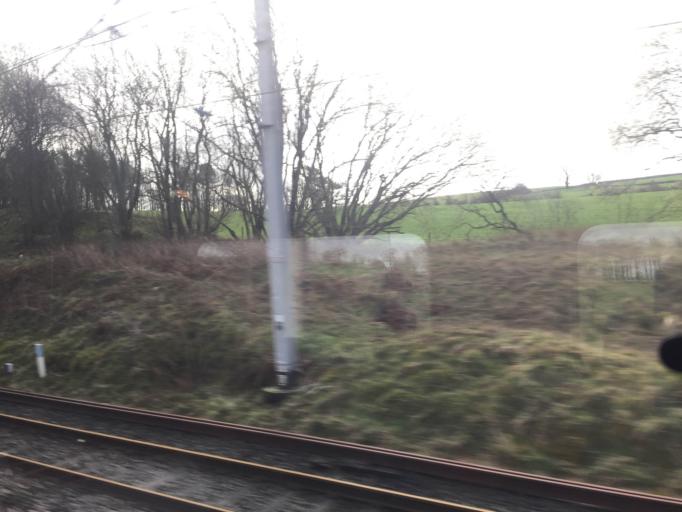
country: GB
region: England
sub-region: Cumbria
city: Sedbergh
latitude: 54.3591
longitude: -2.6156
